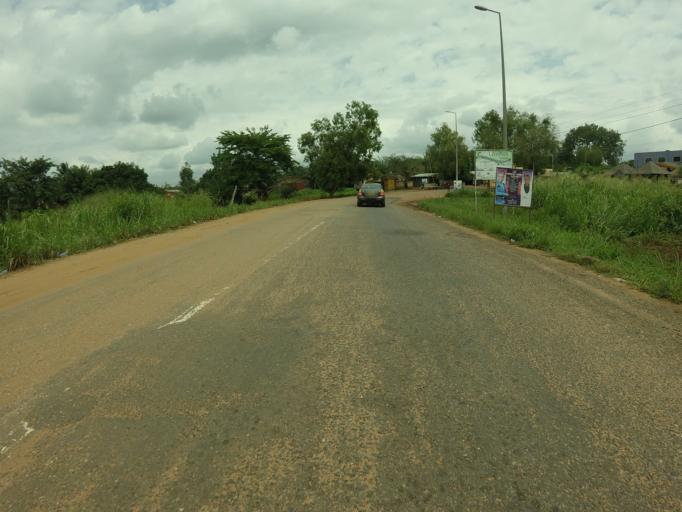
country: GH
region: Volta
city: Ho
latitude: 6.5847
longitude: 0.4630
